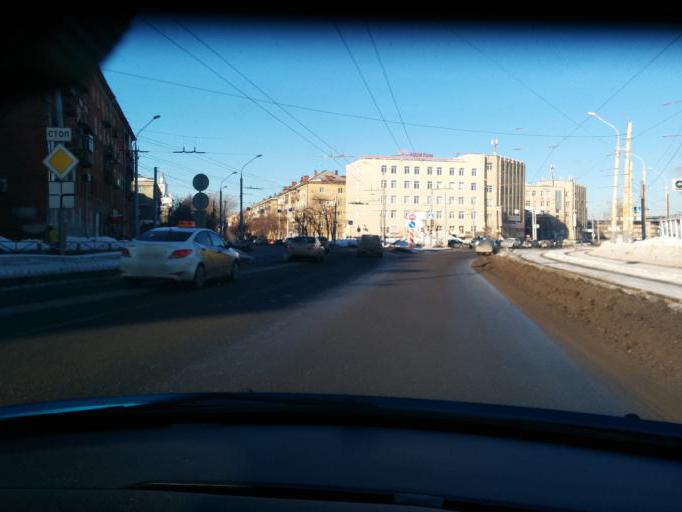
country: RU
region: Perm
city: Perm
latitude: 57.9915
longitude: 56.2574
